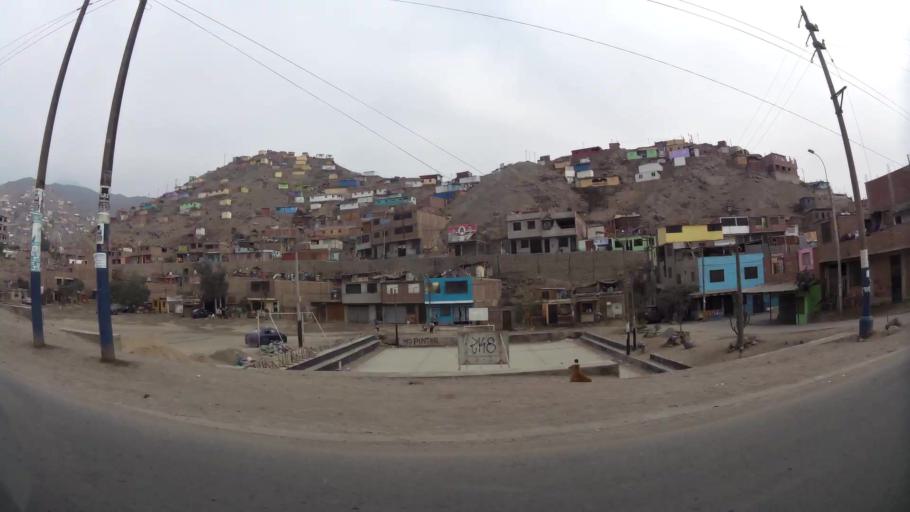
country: PE
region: Lima
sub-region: Lima
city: Independencia
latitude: -11.9801
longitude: -76.9877
